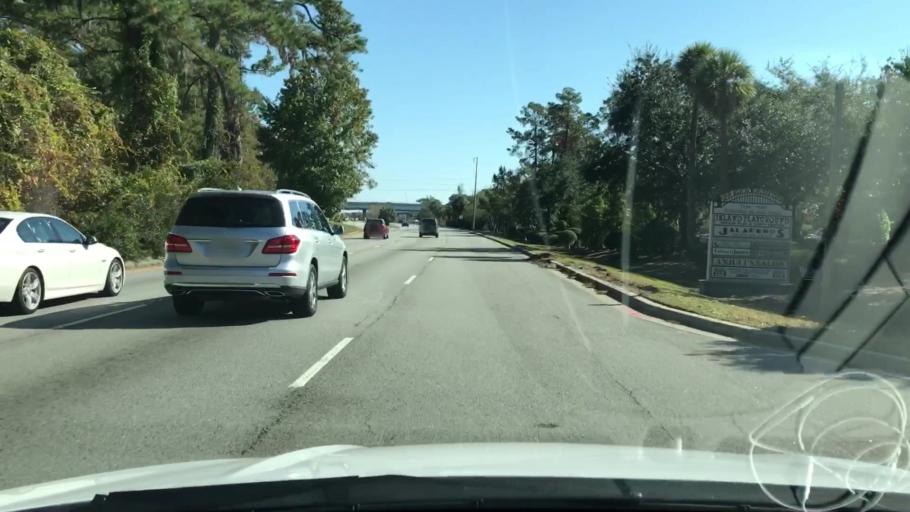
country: US
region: South Carolina
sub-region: Beaufort County
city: Bluffton
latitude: 32.2365
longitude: -80.8079
